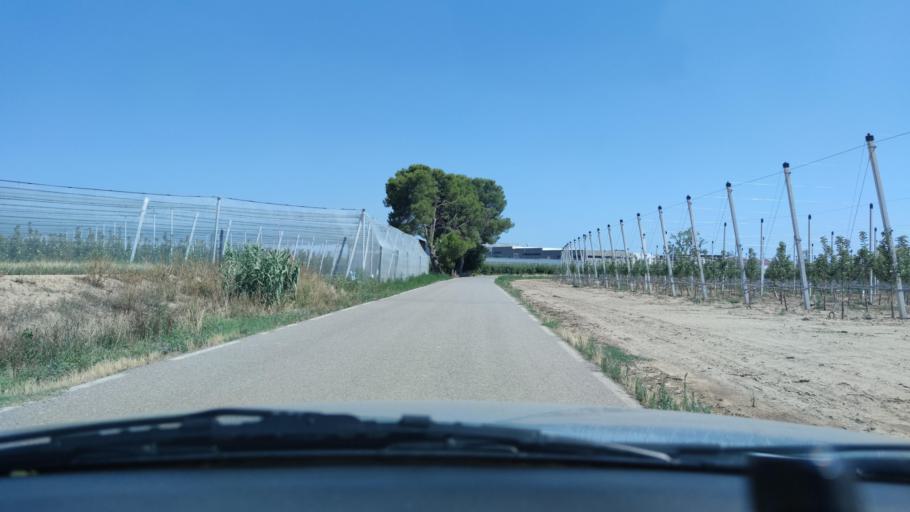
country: ES
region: Catalonia
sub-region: Provincia de Lleida
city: Torrefarrera
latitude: 41.6824
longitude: 0.6267
